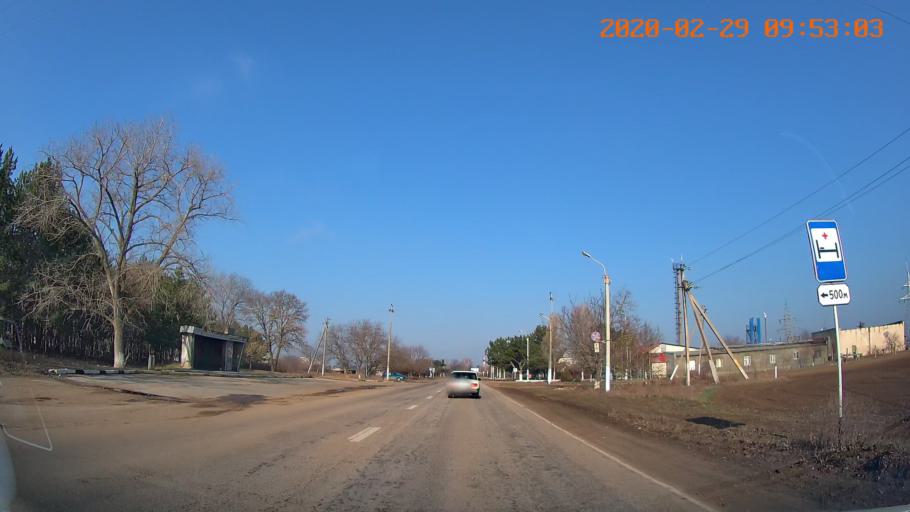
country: MD
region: Telenesti
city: Slobozia
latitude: 46.7197
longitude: 29.7247
